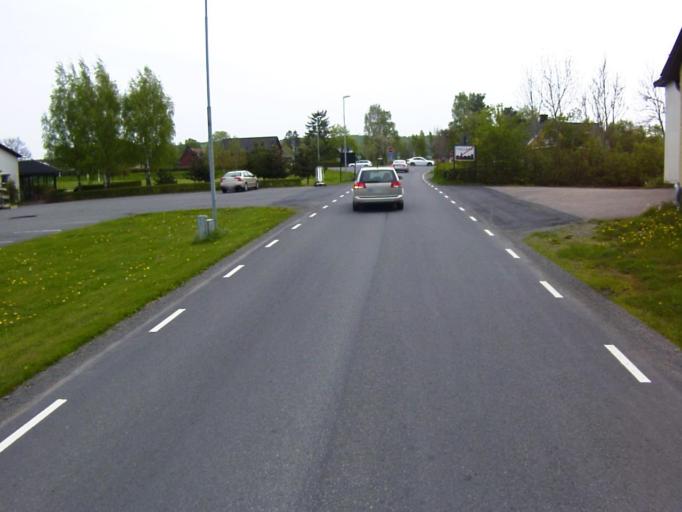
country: SE
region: Skane
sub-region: Kristianstads Kommun
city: Onnestad
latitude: 55.9310
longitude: 13.9547
